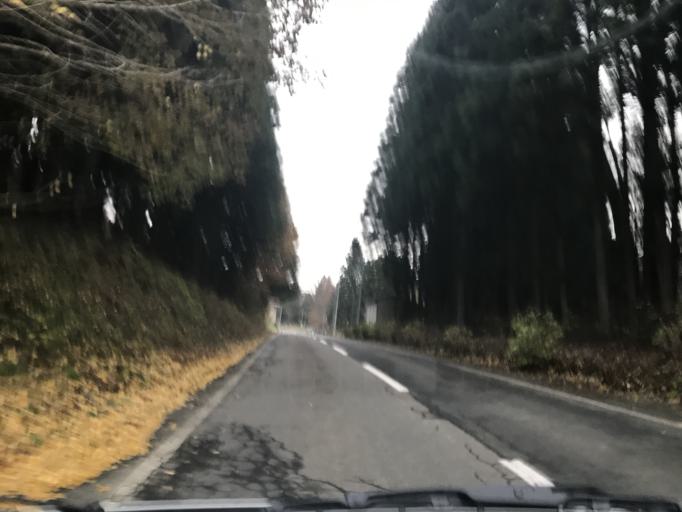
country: JP
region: Iwate
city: Tono
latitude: 39.1895
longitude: 141.3522
